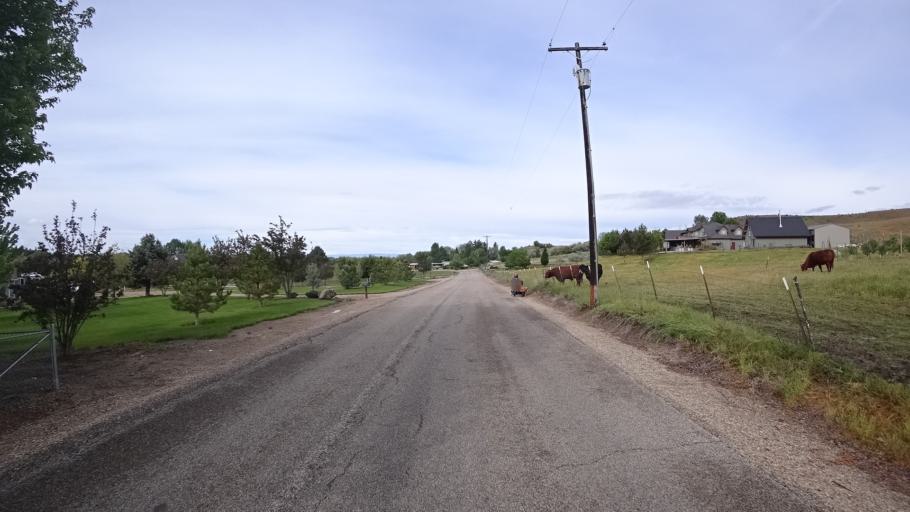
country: US
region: Idaho
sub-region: Ada County
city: Eagle
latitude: 43.7311
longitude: -116.3172
